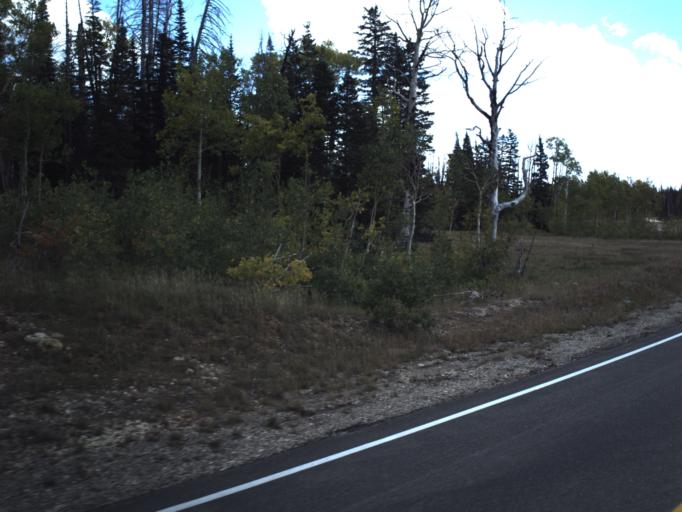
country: US
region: Utah
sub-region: Iron County
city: Parowan
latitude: 37.5425
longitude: -112.7843
